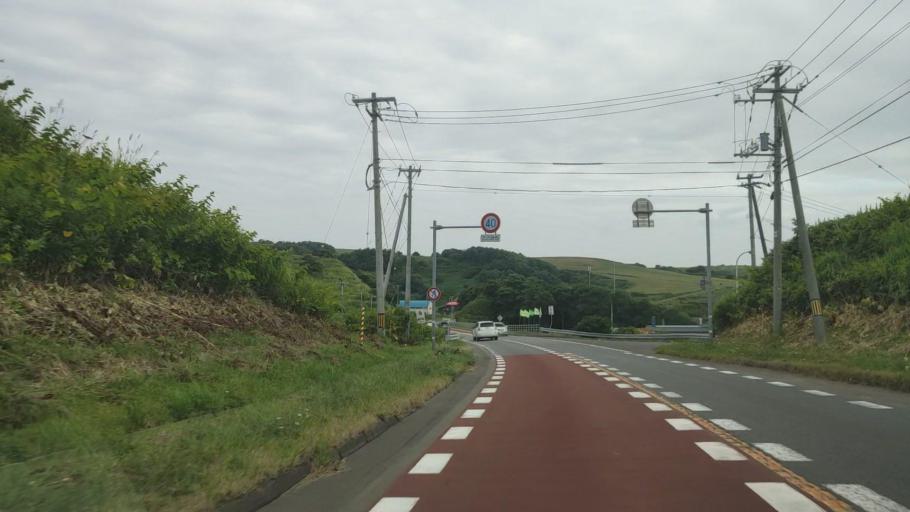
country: JP
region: Hokkaido
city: Ishikari
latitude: 43.3584
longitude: 141.4292
